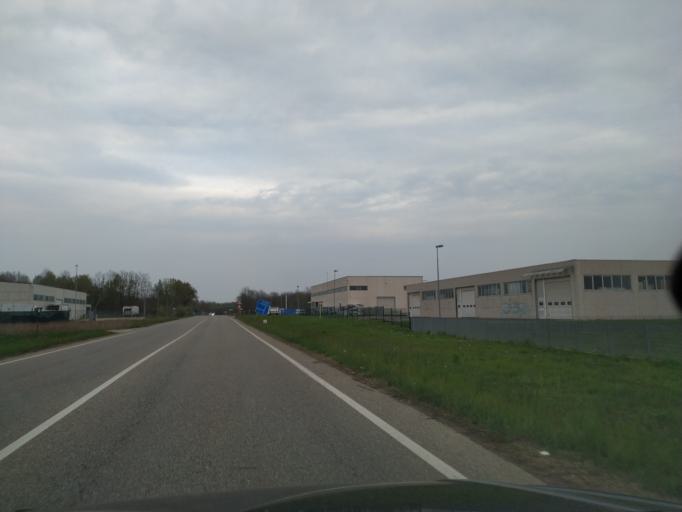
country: IT
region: Piedmont
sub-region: Provincia di Novara
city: Boca
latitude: 45.6562
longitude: 8.4243
